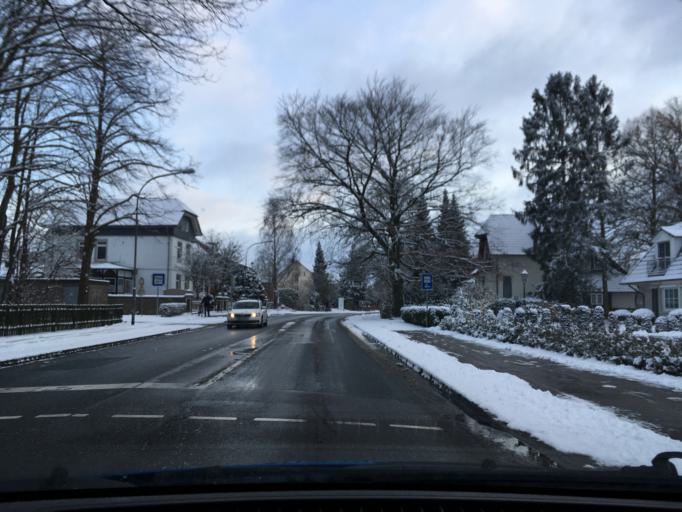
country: DE
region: Lower Saxony
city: Winsen
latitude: 53.3502
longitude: 10.2074
